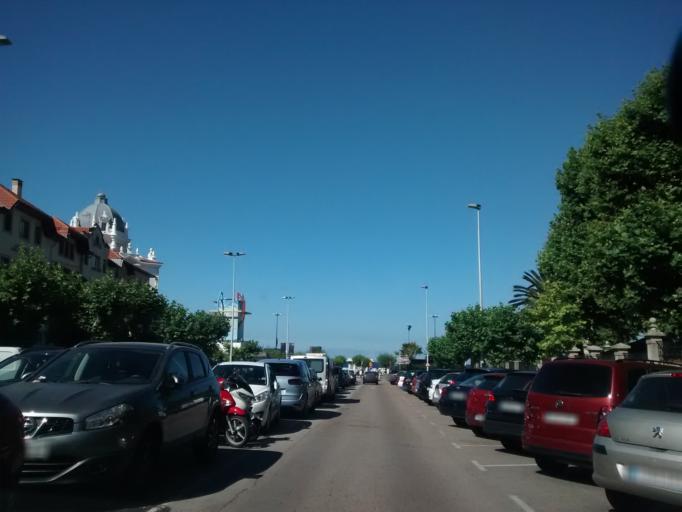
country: ES
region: Cantabria
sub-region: Provincia de Cantabria
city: Santander
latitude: 43.4708
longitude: -3.7827
